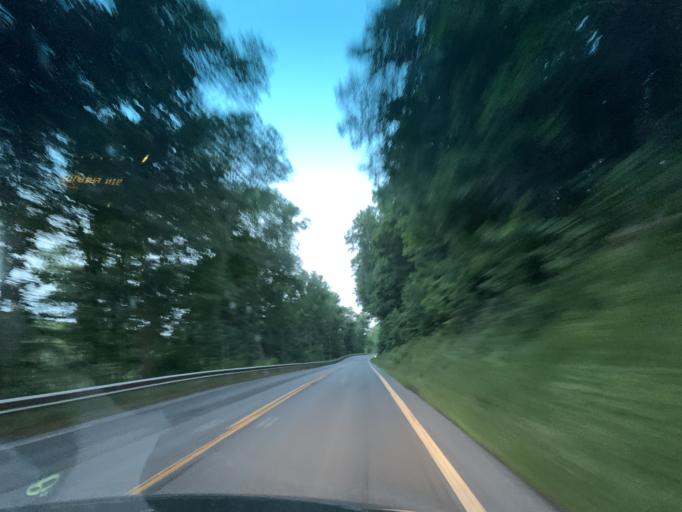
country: US
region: New York
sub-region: Chenango County
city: New Berlin
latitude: 42.6618
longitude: -75.3320
